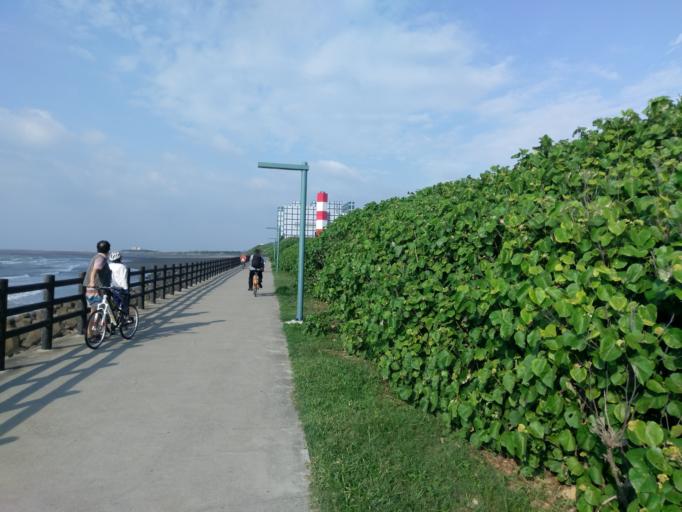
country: TW
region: Taiwan
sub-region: Hsinchu
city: Hsinchu
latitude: 24.8301
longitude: 120.9129
